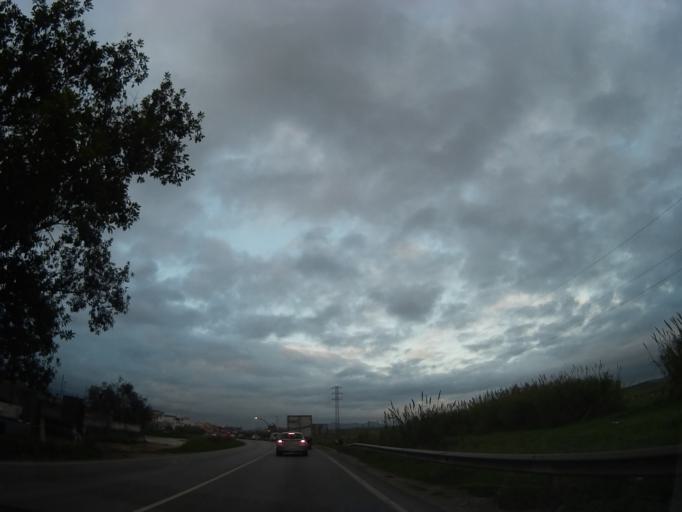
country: ES
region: Andalusia
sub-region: Provincia de Malaga
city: Alhaurin de la Torre
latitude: 36.7069
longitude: -4.5027
